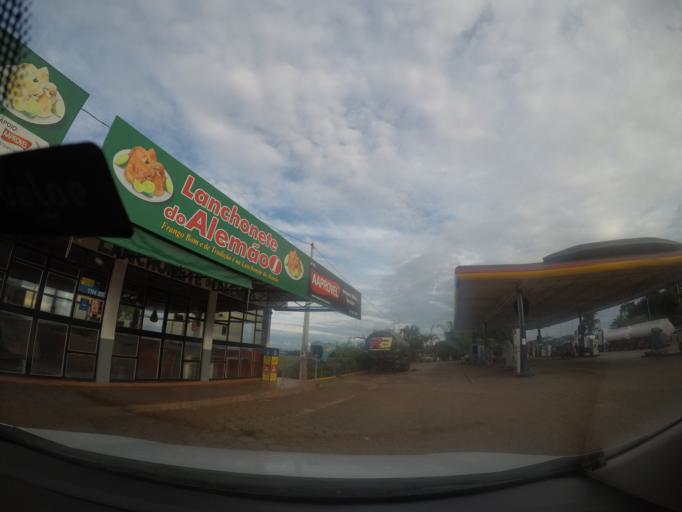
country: BR
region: Goias
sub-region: Goiania
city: Goiania
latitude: -16.6247
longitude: -49.3531
